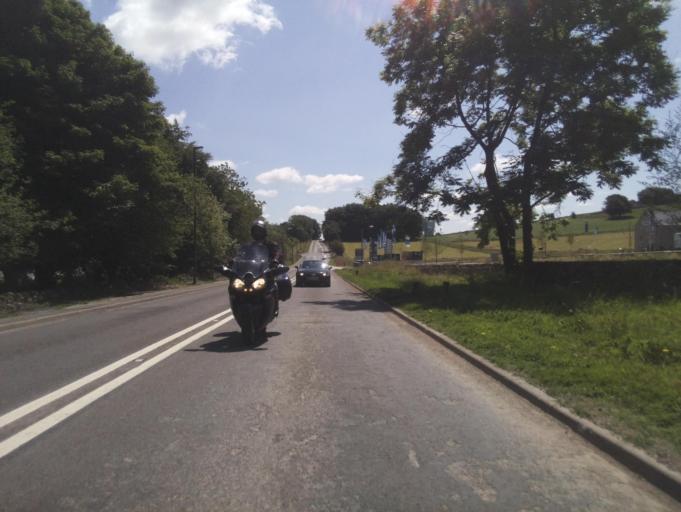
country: GB
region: England
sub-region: Derbyshire
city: Buxton
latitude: 53.2436
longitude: -1.9000
